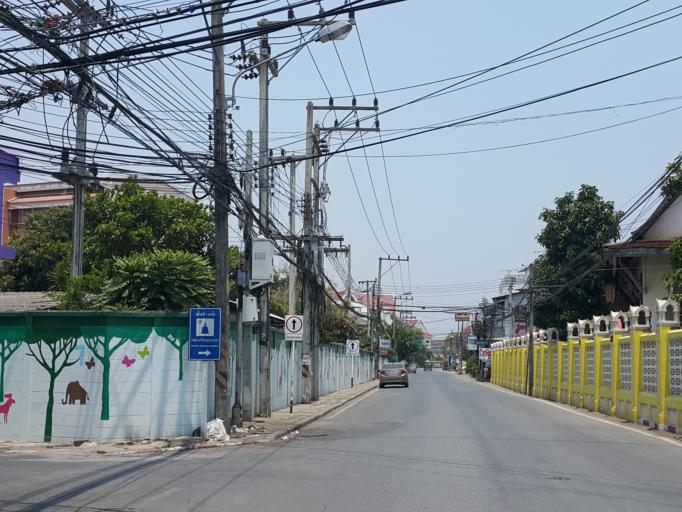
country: TH
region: Phitsanulok
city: Phitsanulok
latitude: 16.8191
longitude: 100.2617
